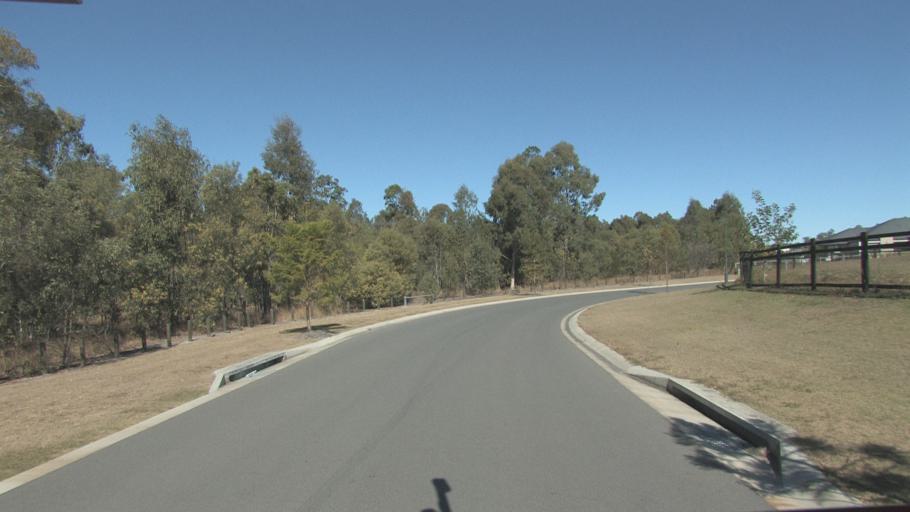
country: AU
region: Queensland
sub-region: Logan
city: North Maclean
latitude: -27.7538
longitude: 152.9526
